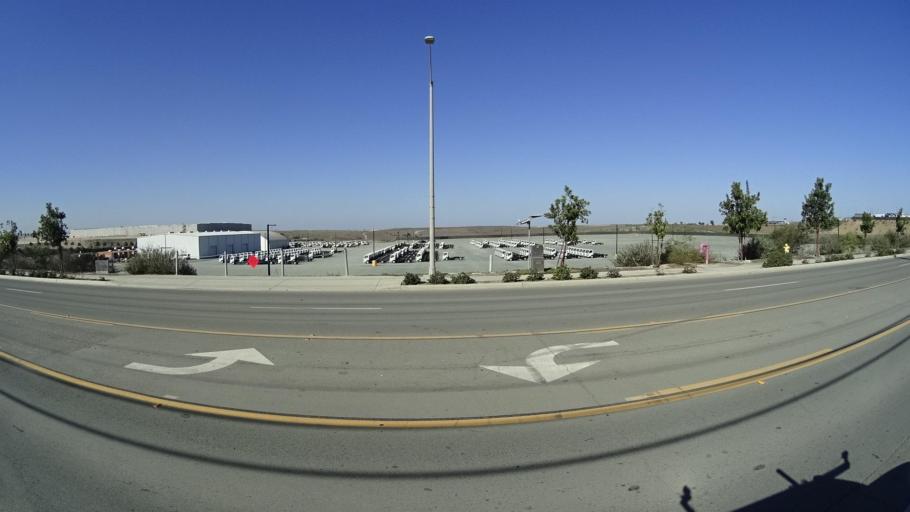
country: MX
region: Baja California
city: Tijuana
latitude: 32.5730
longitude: -116.9191
